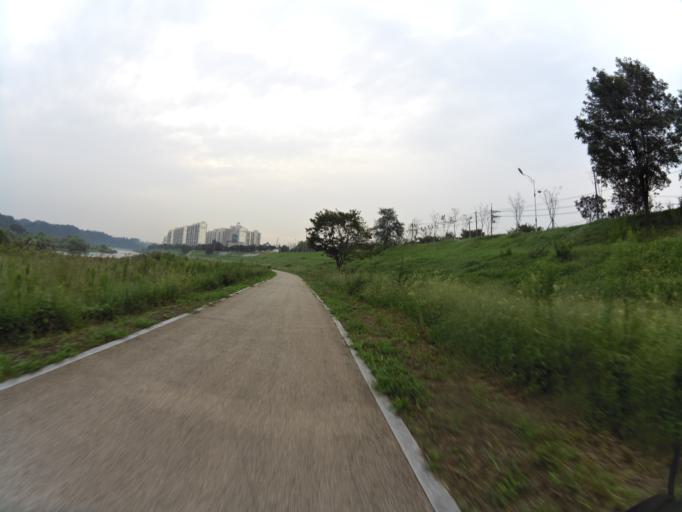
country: KR
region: Gyeongsangbuk-do
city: Gyeongsan-si
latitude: 35.8744
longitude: 128.6764
